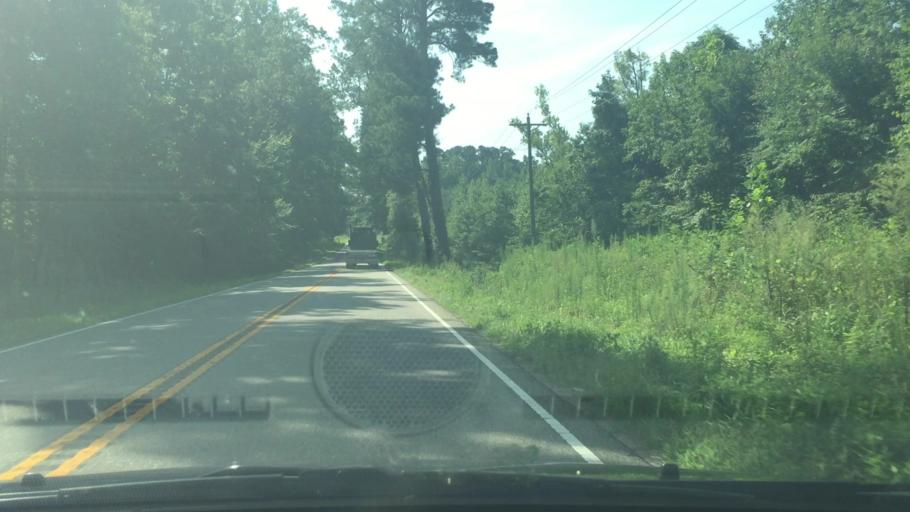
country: US
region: Virginia
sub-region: Sussex County
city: Sussex
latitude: 37.0090
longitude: -77.2719
